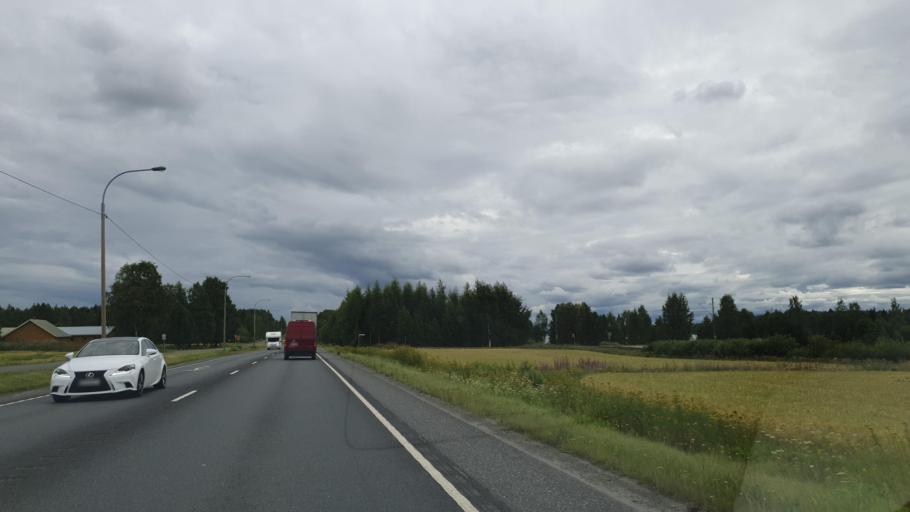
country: FI
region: Northern Savo
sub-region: Ylae-Savo
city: Lapinlahti
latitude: 63.4539
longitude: 27.3175
